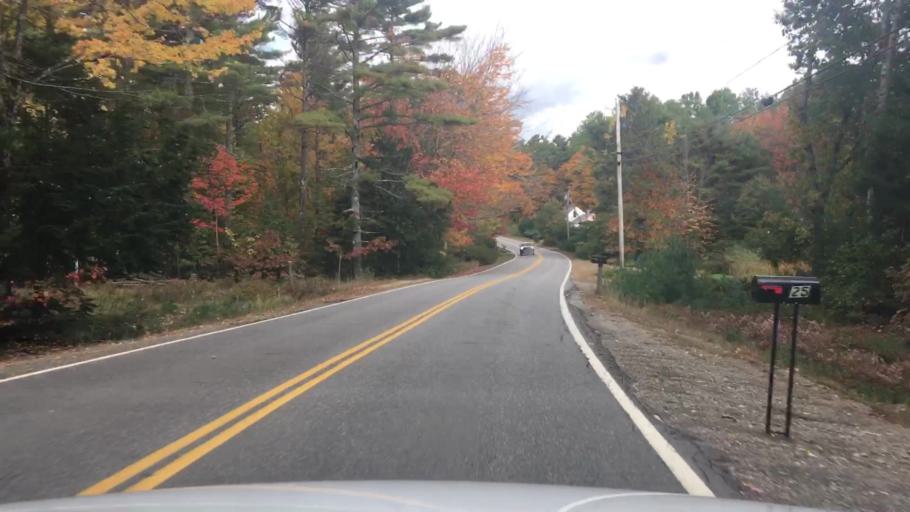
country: US
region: Maine
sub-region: Knox County
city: Hope
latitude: 44.2631
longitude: -69.1344
